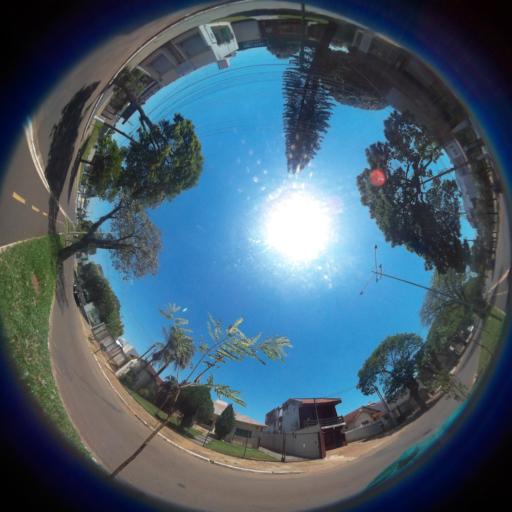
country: BR
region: Mato Grosso do Sul
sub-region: Ponta Pora
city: Ponta Pora
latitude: -22.5373
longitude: -55.7220
